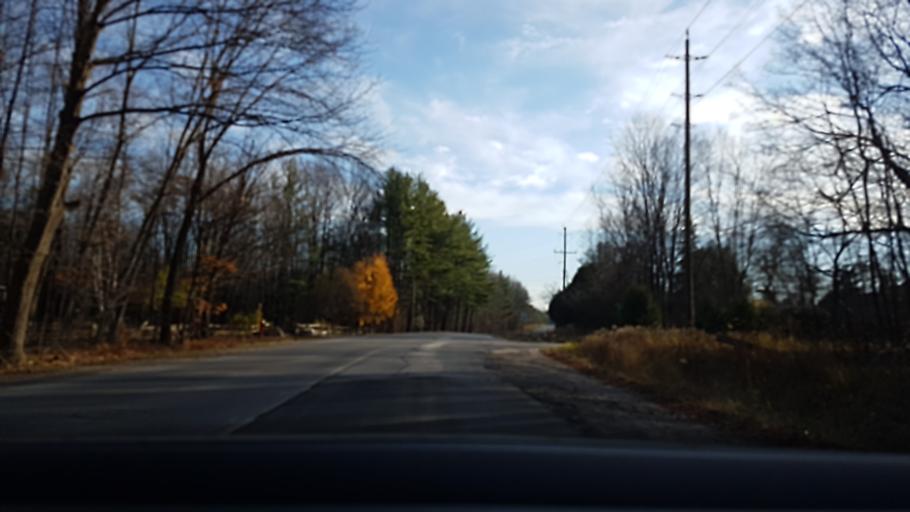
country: CA
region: Ontario
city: Barrie
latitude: 44.3725
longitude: -79.5521
